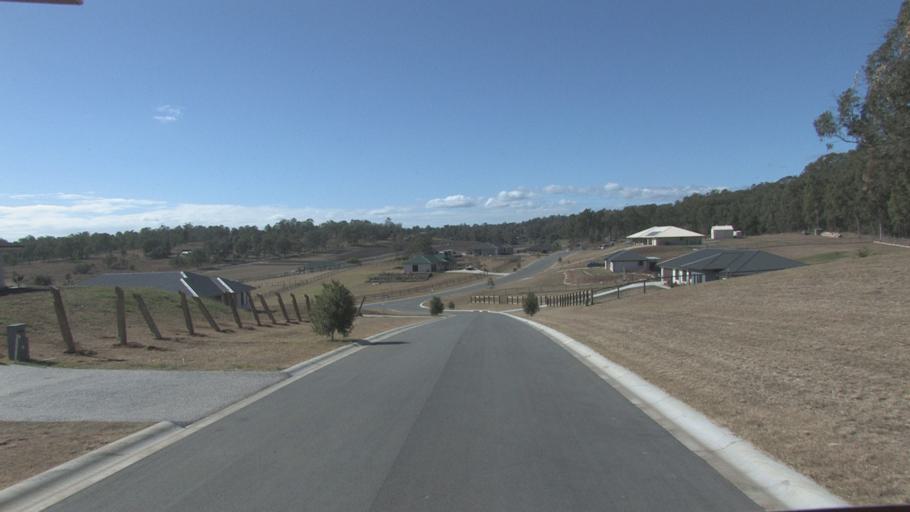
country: AU
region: Queensland
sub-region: Logan
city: Cedar Vale
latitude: -27.8899
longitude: 152.9817
